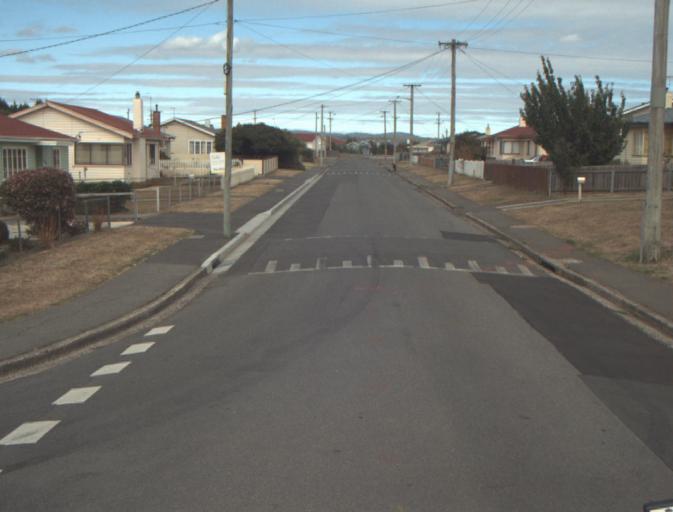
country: AU
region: Tasmania
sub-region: Launceston
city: Mayfield
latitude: -41.3823
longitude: 147.1308
